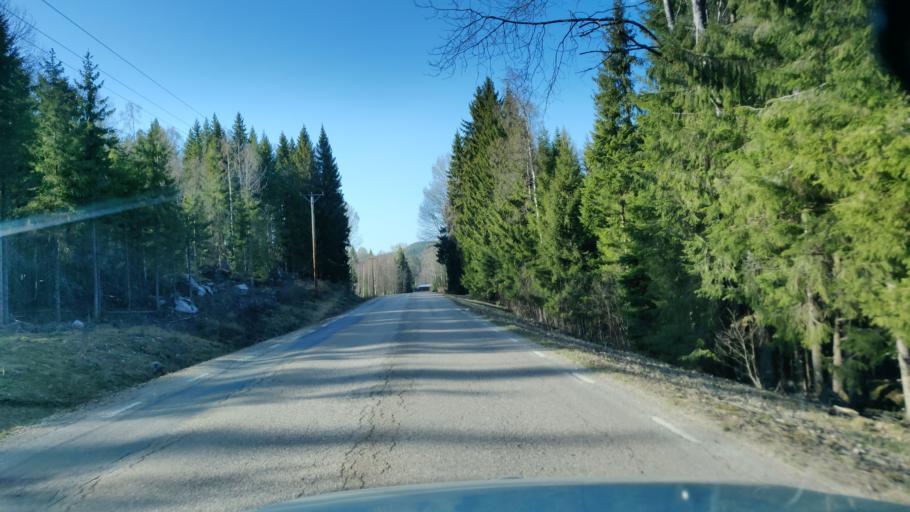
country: SE
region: Vaermland
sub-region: Munkfors Kommun
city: Munkfors
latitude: 59.9714
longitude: 13.4172
